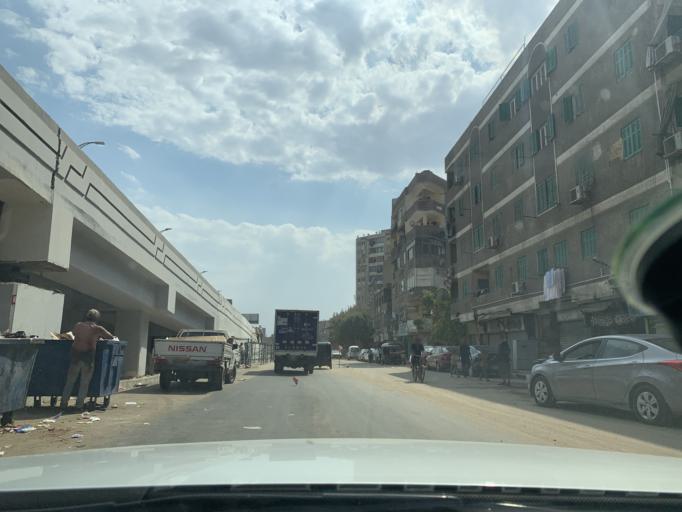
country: EG
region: Muhafazat al Qahirah
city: Cairo
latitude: 30.1148
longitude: 31.3041
